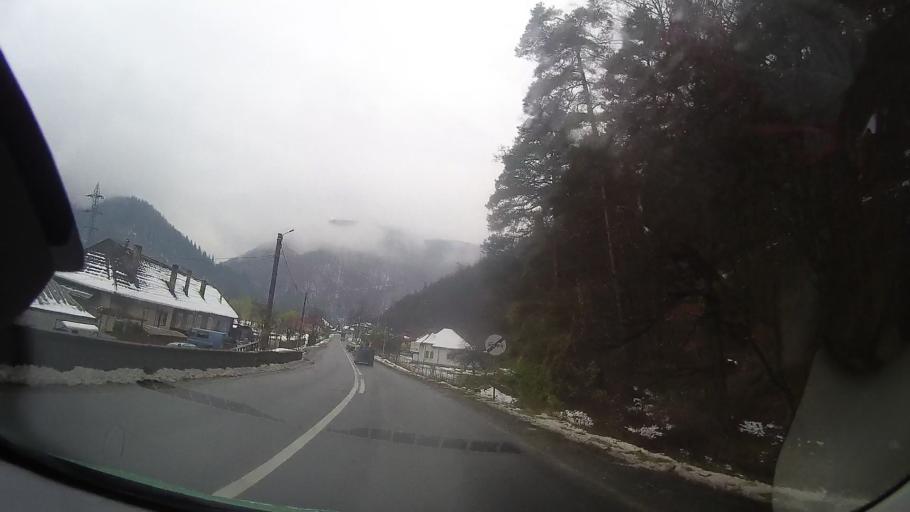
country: RO
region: Neamt
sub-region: Comuna Tarcau
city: Tarcau
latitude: 46.8931
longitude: 26.1322
